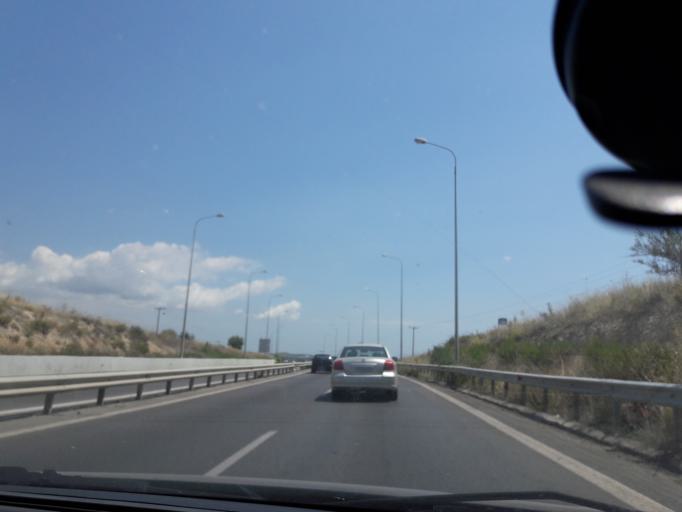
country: GR
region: Central Macedonia
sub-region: Nomos Chalkidikis
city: Nea Plagia
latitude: 40.2847
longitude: 23.1527
